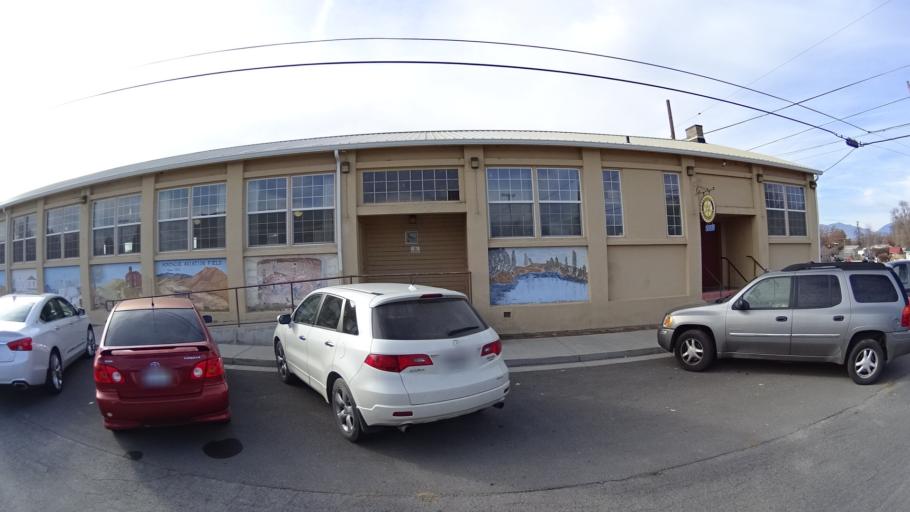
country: US
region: California
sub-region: Siskiyou County
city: Montague
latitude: 41.7272
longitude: -122.5296
